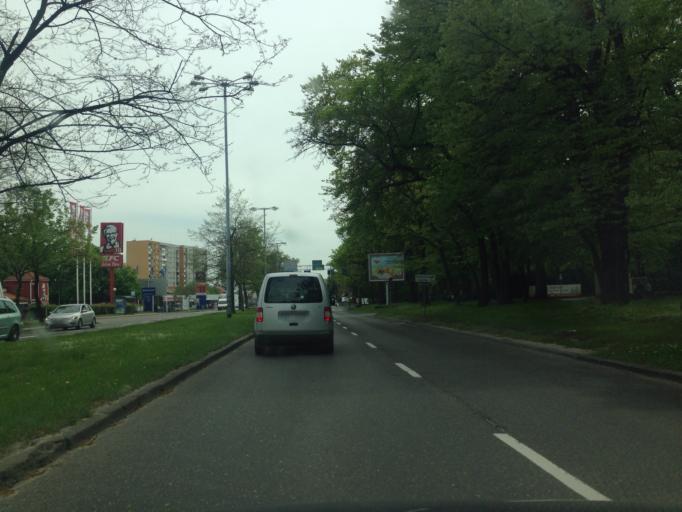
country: PL
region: Pomeranian Voivodeship
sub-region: Sopot
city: Sopot
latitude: 54.4256
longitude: 18.5630
